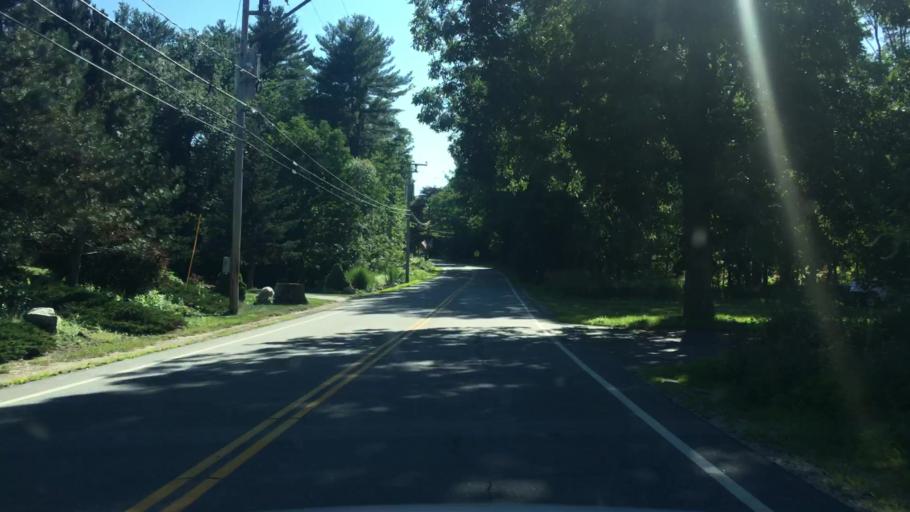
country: US
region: New Hampshire
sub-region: Rockingham County
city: Brentwood
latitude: 42.9857
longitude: -71.0608
